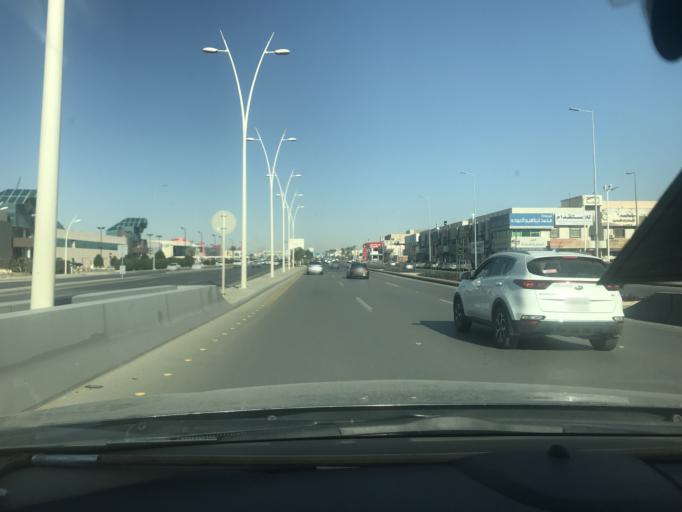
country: SA
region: Ar Riyad
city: Riyadh
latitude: 24.7390
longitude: 46.6841
